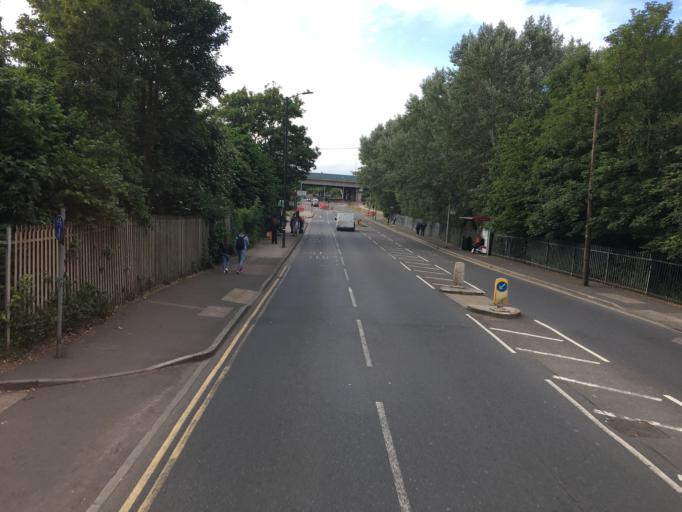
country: GB
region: England
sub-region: Greater London
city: East Ham
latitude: 51.5180
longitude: 0.0600
